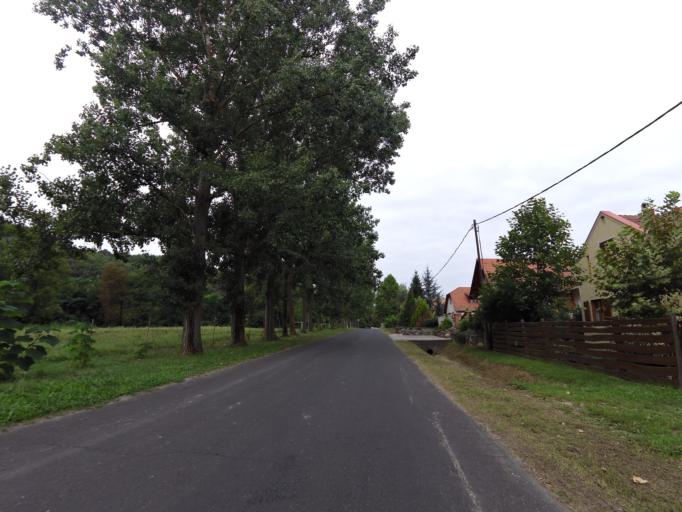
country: HU
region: Zala
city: Vonyarcvashegy
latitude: 46.8430
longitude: 17.3513
